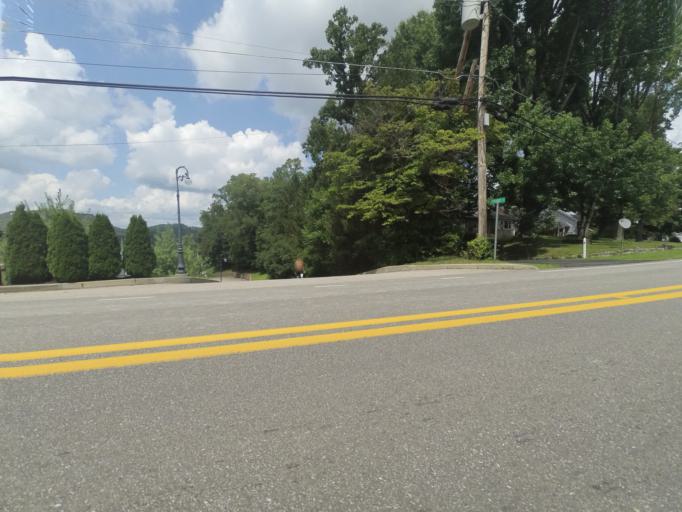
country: US
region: West Virginia
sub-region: Cabell County
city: Pea Ridge
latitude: 38.4093
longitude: -82.3450
